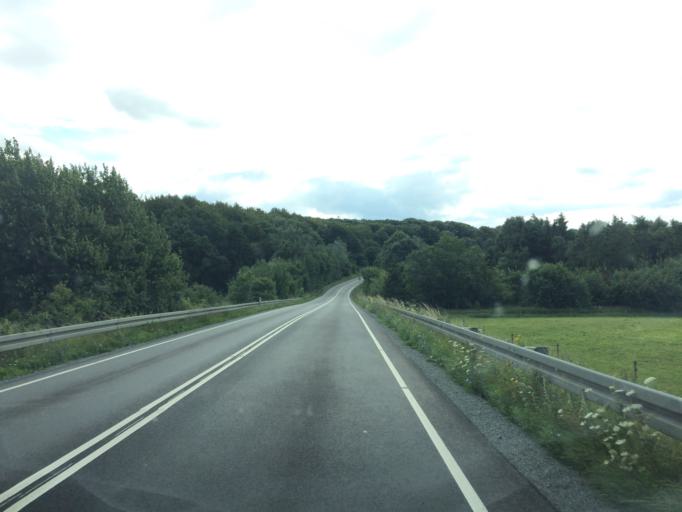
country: DK
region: South Denmark
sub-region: Faaborg-Midtfyn Kommune
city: Faaborg
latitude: 55.1423
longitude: 10.2641
